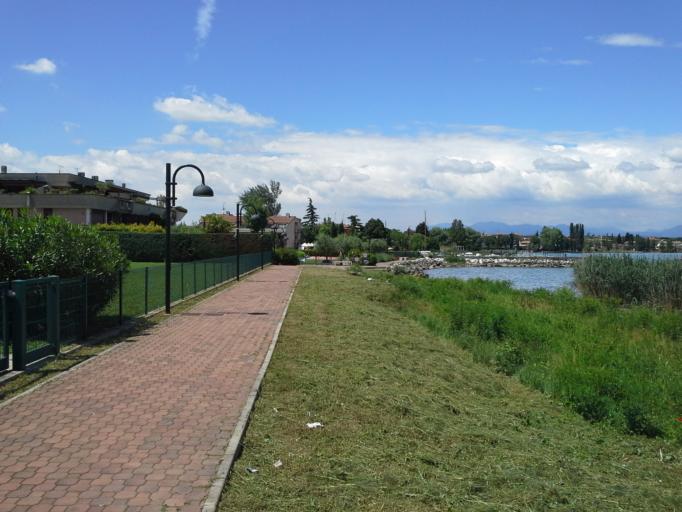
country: IT
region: Lombardy
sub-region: Provincia di Brescia
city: San Martino della Battaglia
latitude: 45.4633
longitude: 10.6180
